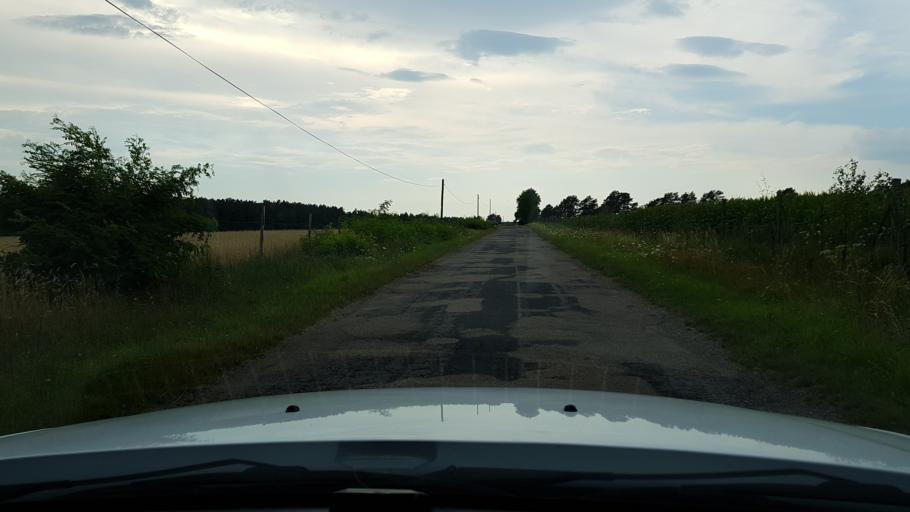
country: PL
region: West Pomeranian Voivodeship
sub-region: Powiat drawski
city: Czaplinek
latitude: 53.4330
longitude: 16.2933
